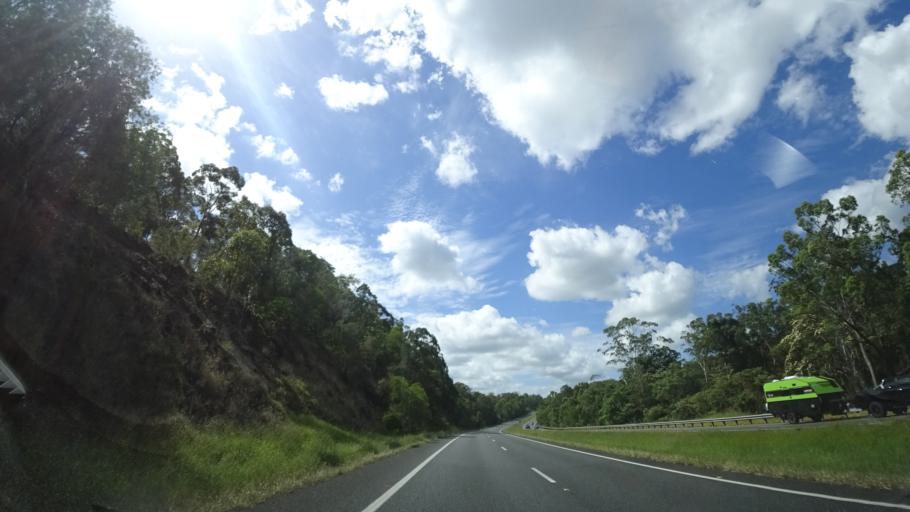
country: AU
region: Queensland
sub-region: Sunshine Coast
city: Nambour
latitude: -26.6079
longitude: 152.9744
